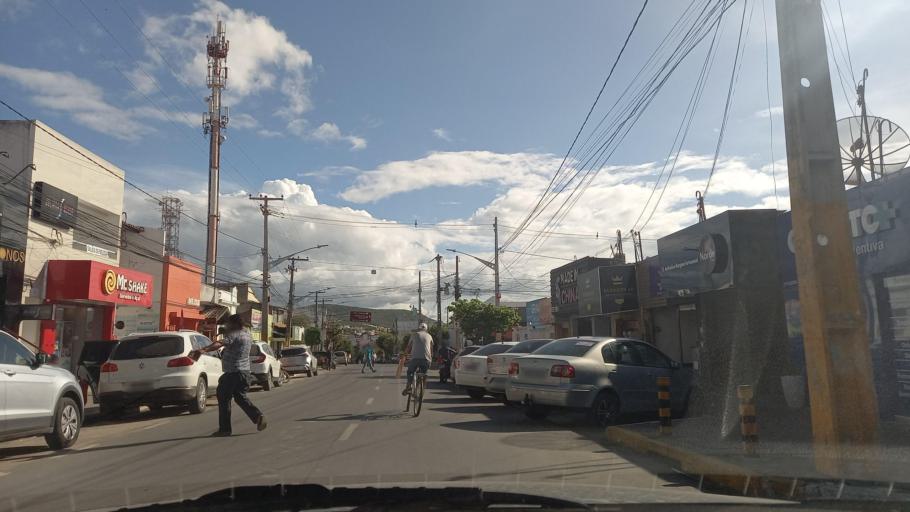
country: BR
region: Pernambuco
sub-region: Gravata
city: Gravata
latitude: -8.1999
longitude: -35.5641
